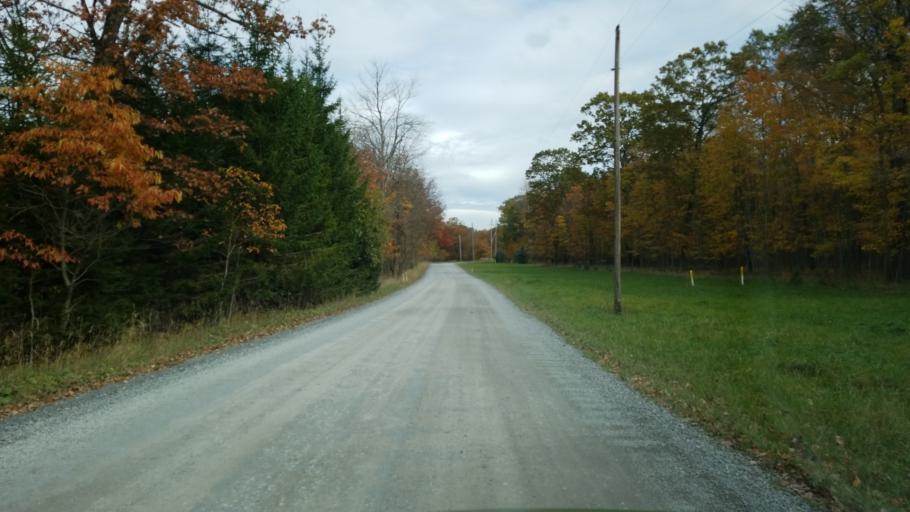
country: US
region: Pennsylvania
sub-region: Clearfield County
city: Clearfield
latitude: 41.1524
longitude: -78.4653
